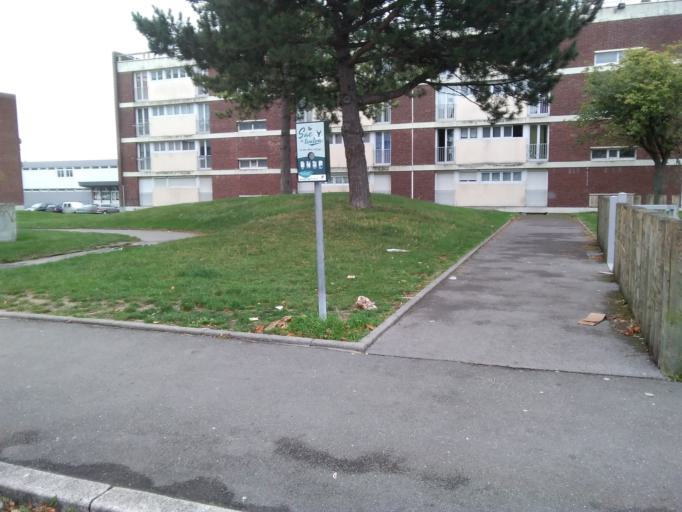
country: FR
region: Picardie
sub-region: Departement de la Somme
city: Rivery
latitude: 49.9104
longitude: 2.3119
